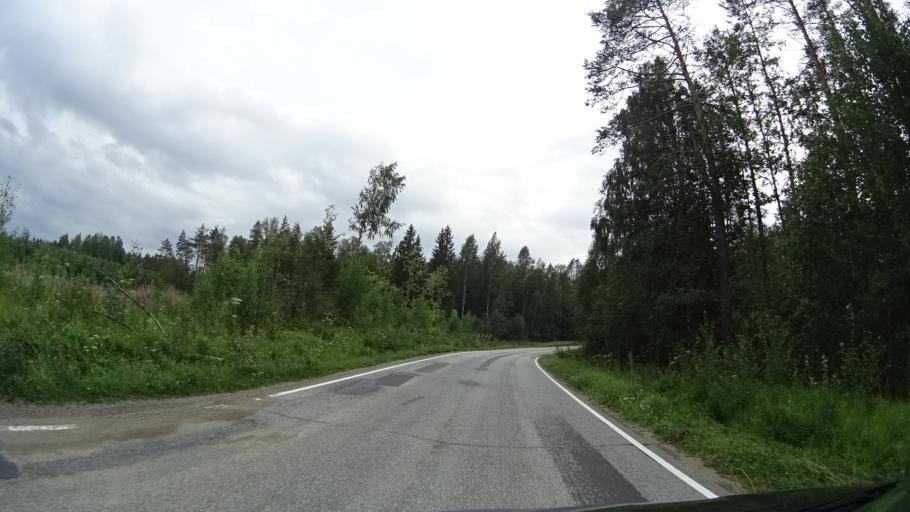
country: FI
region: Southern Savonia
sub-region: Savonlinna
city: Punkaharju
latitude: 61.7475
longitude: 29.5028
